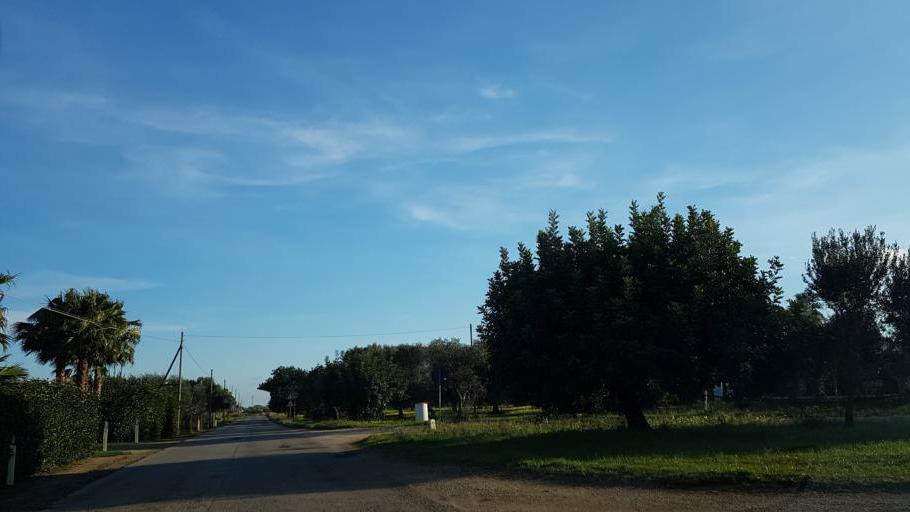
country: IT
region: Apulia
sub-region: Provincia di Brindisi
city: San Vito dei Normanni
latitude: 40.6711
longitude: 17.7778
